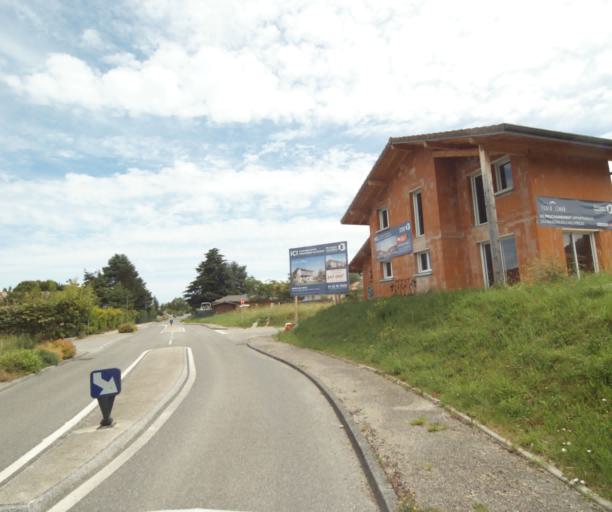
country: FR
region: Rhone-Alpes
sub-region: Departement de la Haute-Savoie
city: Anthy-sur-Leman
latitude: 46.3527
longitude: 6.4109
